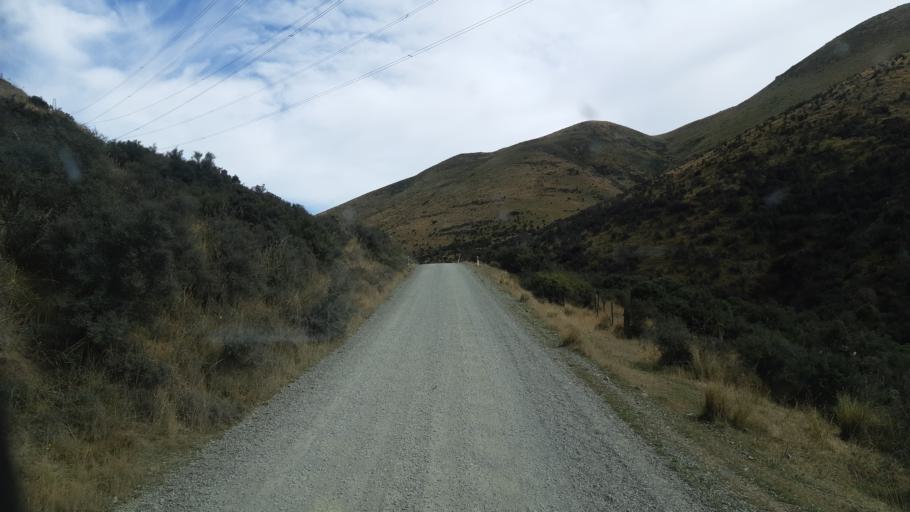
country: NZ
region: Canterbury
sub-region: Timaru District
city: Pleasant Point
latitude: -44.1933
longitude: 170.6268
